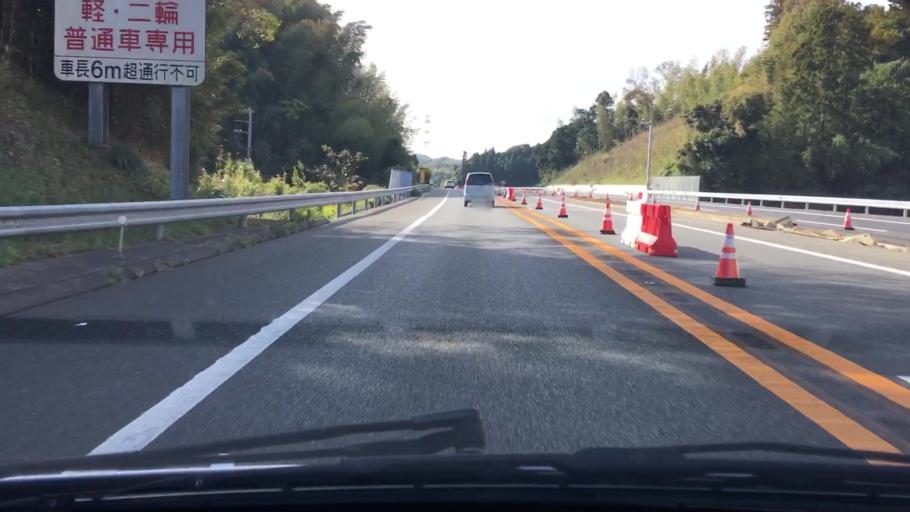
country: JP
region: Chiba
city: Kimitsu
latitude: 35.2921
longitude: 139.9310
